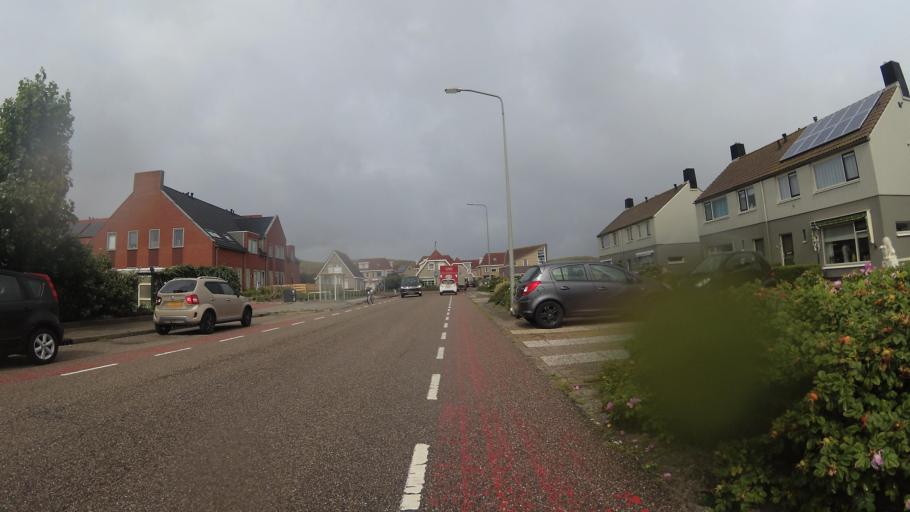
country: NL
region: North Holland
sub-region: Gemeente Schagen
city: Schagen
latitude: 52.8401
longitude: 4.6973
